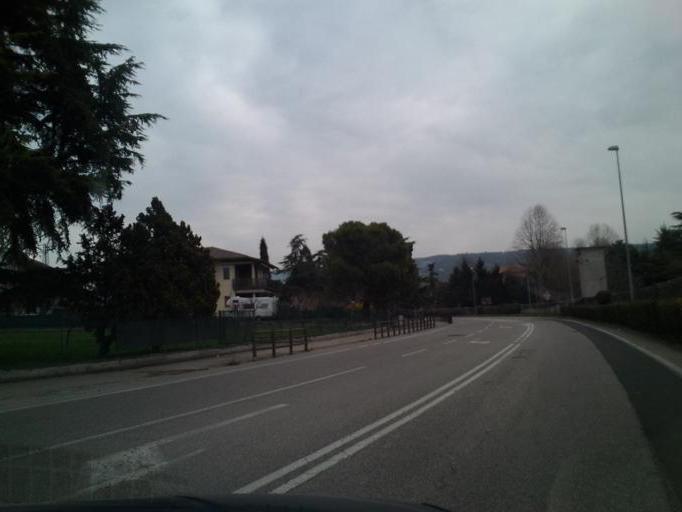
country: IT
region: Veneto
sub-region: Provincia di Verona
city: Montorio
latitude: 45.4539
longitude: 11.0576
